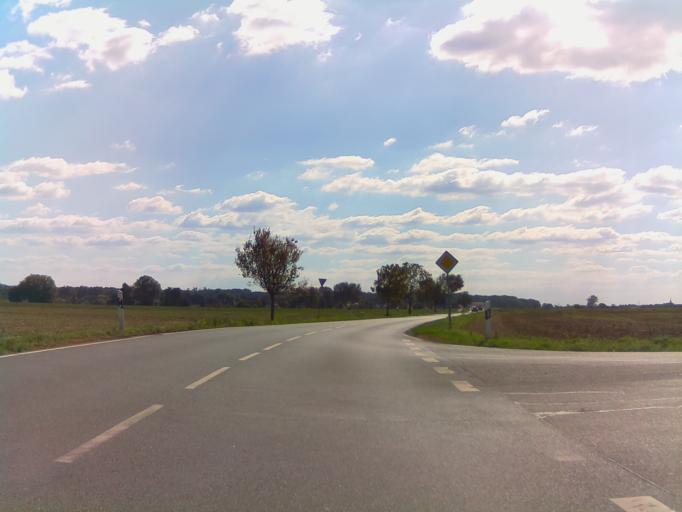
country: DE
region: Hesse
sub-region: Regierungsbezirk Darmstadt
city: Alsbach-Hahnlein
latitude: 49.7305
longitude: 8.5735
